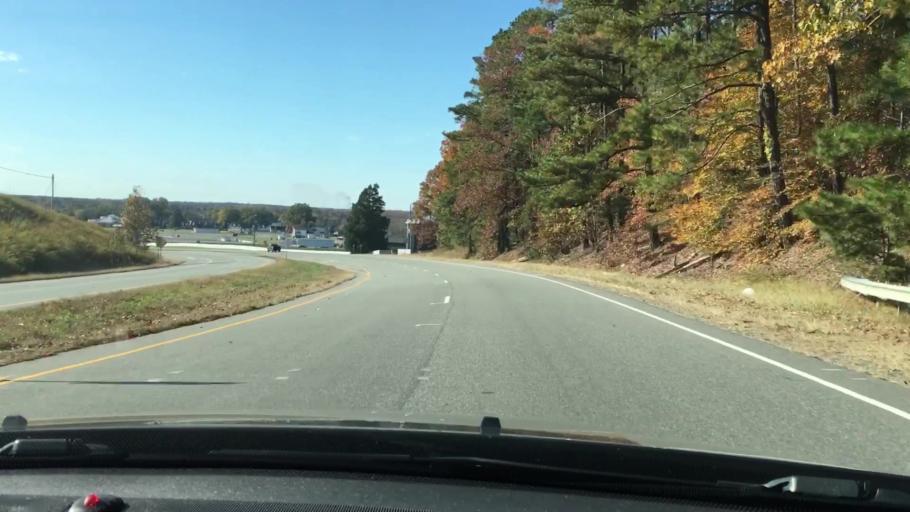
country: US
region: Virginia
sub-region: Hanover County
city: Hanover
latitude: 37.8513
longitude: -77.4104
